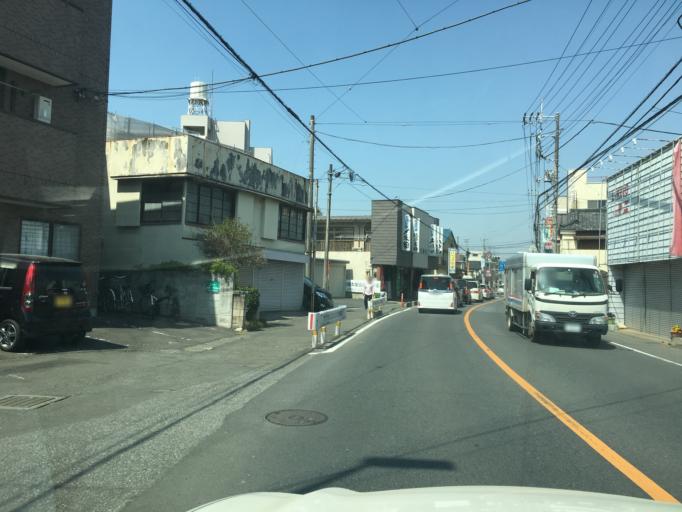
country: JP
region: Saitama
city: Sayama
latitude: 35.8333
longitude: 139.4294
